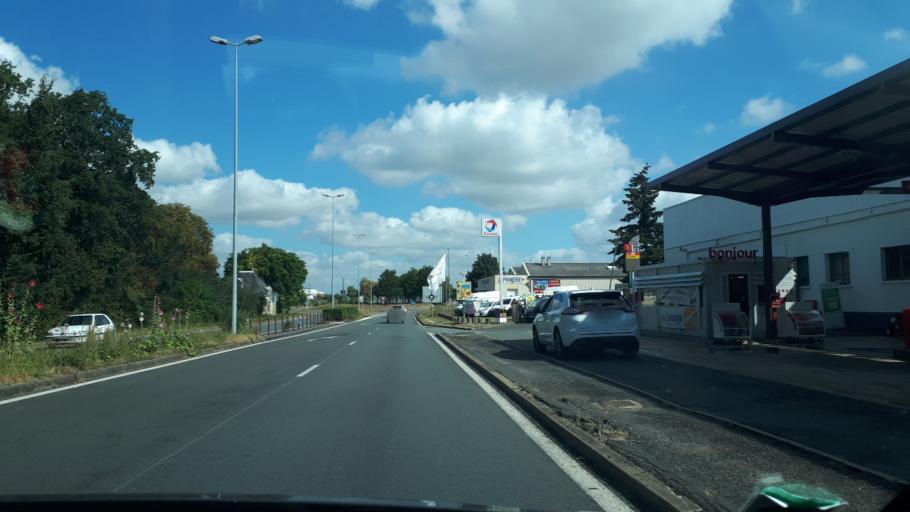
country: FR
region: Centre
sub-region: Departement du Loir-et-Cher
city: Saint-Ouen
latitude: 47.8165
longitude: 1.0759
